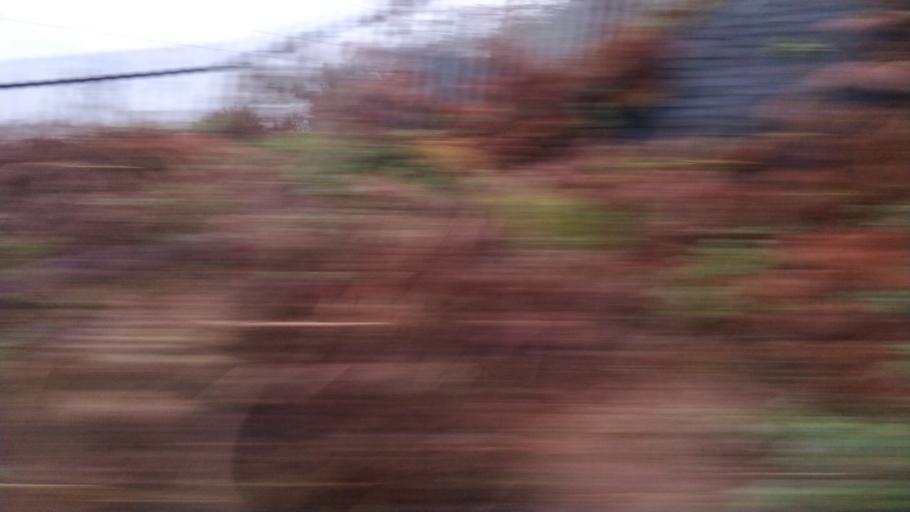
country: GB
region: England
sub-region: Borough of Wigan
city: Tyldesley
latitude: 53.5279
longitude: -2.4636
